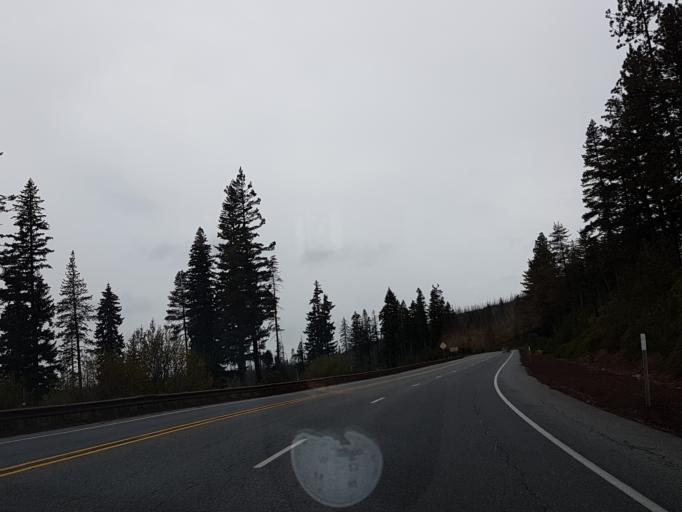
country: US
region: Oregon
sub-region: Deschutes County
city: Sisters
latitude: 44.4231
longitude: -121.8046
